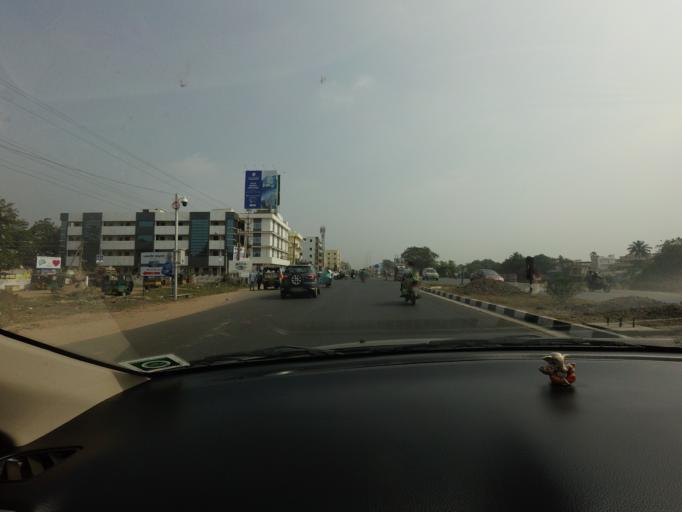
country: IN
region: Andhra Pradesh
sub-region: Krishna
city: Yanamalakuduru
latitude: 16.4802
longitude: 80.6972
